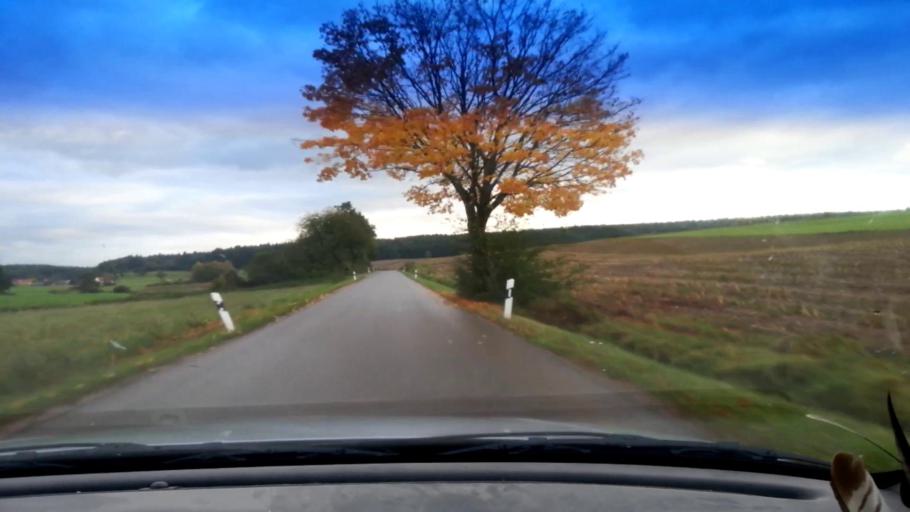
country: DE
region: Bavaria
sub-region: Upper Franconia
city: Burgebrach
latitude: 49.8140
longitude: 10.6895
